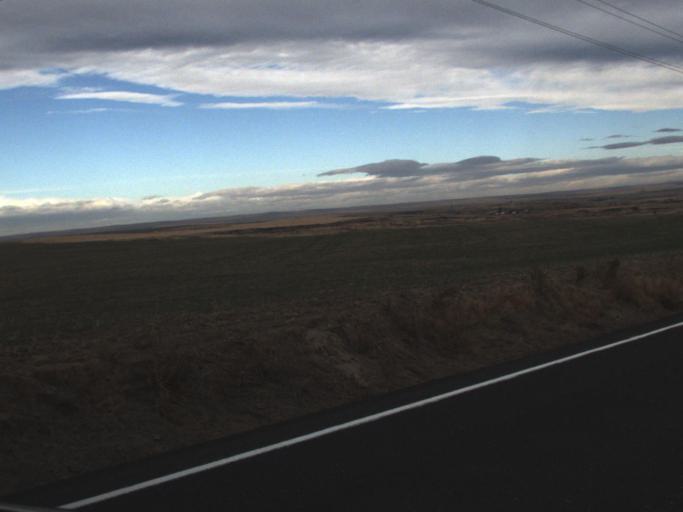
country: US
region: Washington
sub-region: Okanogan County
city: Coulee Dam
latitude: 47.6578
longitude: -118.7213
